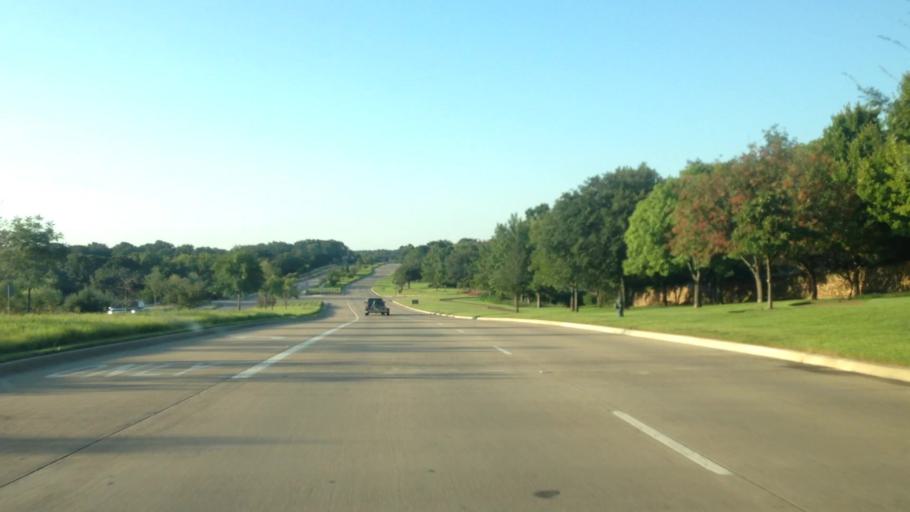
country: US
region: Texas
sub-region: Denton County
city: Trophy Club
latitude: 32.9728
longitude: -97.1864
